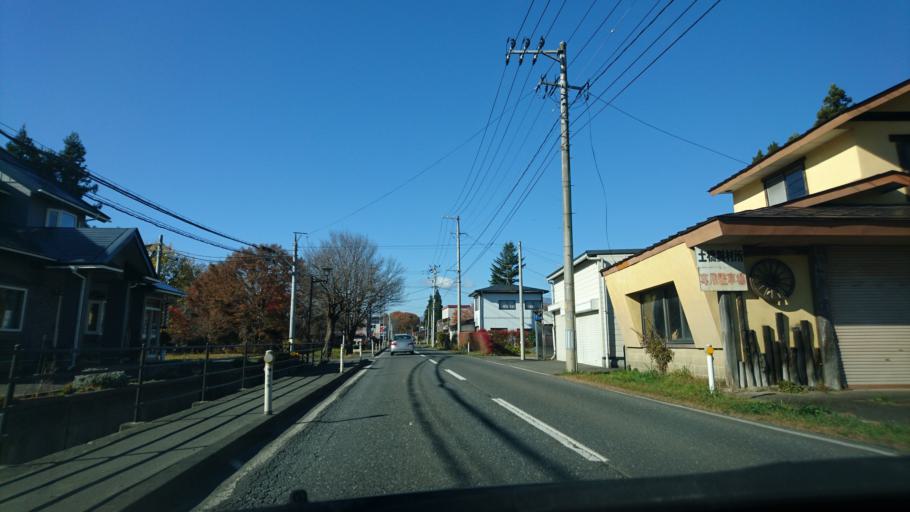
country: JP
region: Iwate
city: Mizusawa
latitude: 39.1293
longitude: 141.0315
